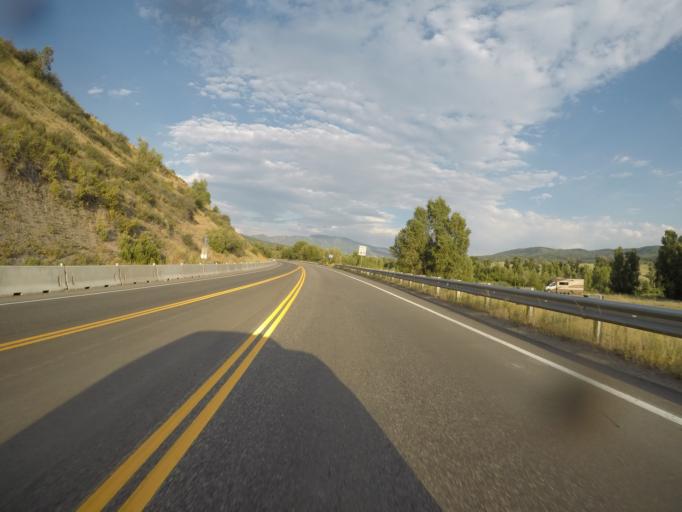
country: US
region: Colorado
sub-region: Routt County
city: Steamboat Springs
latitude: 40.5045
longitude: -106.8752
